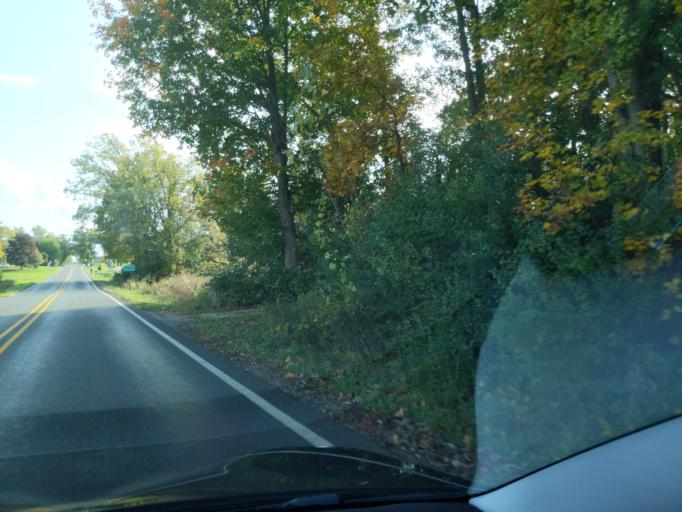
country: US
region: Michigan
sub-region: Jackson County
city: Jackson
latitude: 42.3350
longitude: -84.4629
